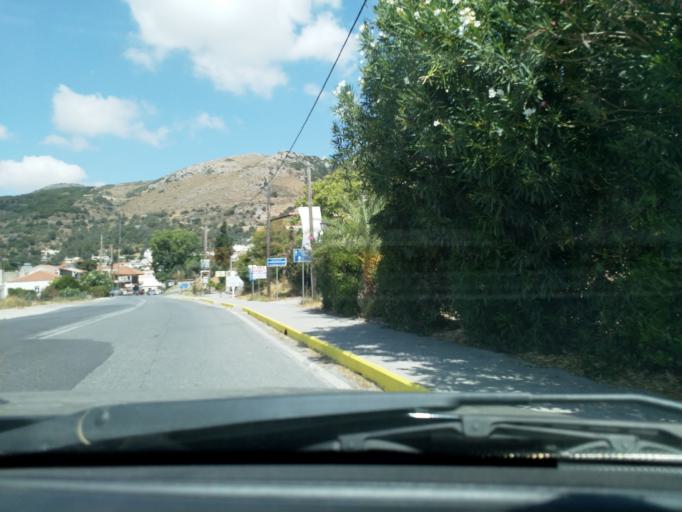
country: GR
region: Crete
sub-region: Nomos Rethymnis
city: Agia Foteini
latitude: 35.2145
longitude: 24.5354
